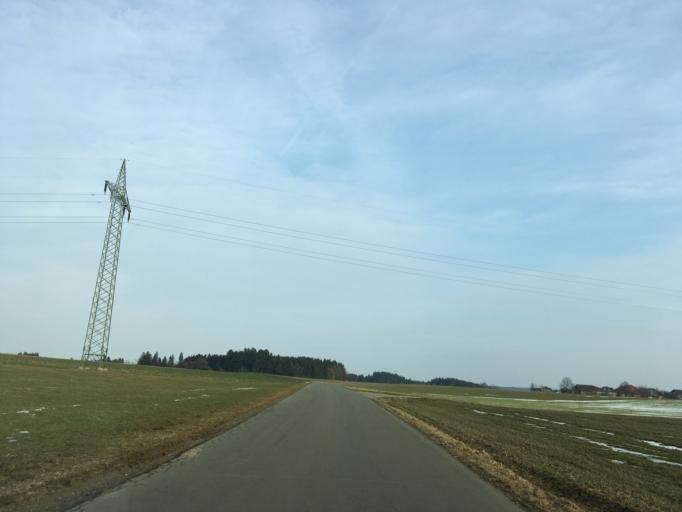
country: DE
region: Bavaria
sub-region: Upper Bavaria
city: Sochtenau
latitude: 47.9447
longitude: 12.2260
